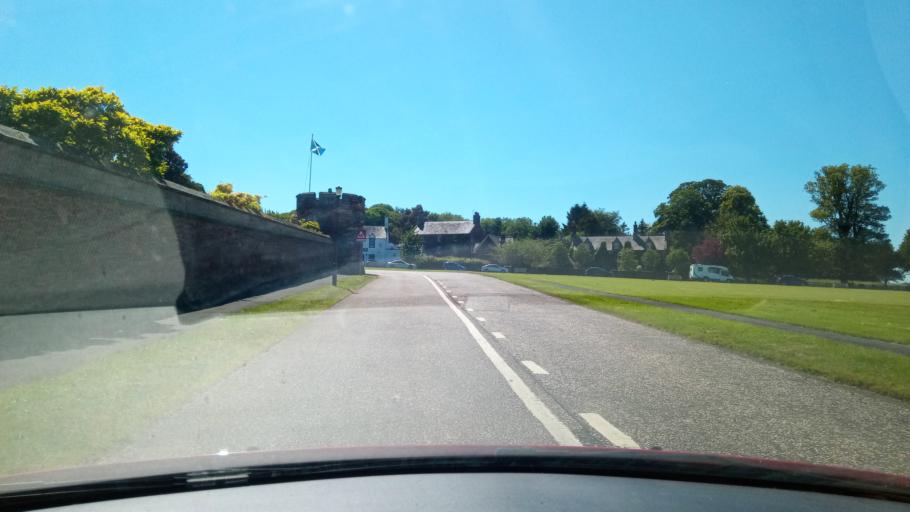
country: GB
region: Scotland
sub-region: East Lothian
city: Gullane
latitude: 56.0464
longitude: -2.7801
